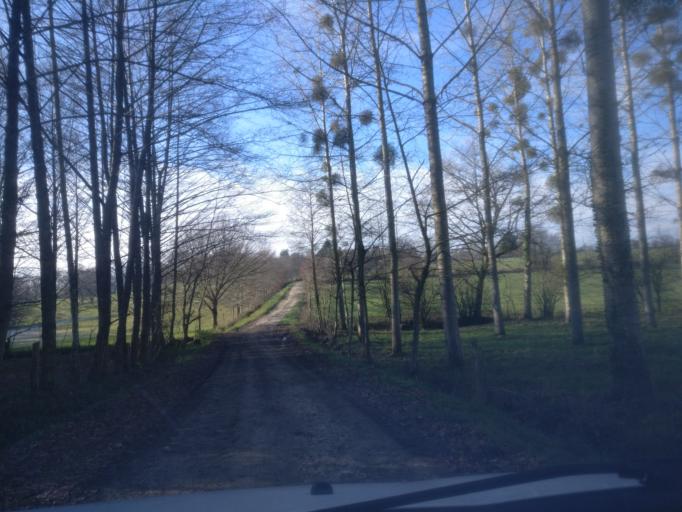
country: FR
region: Brittany
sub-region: Departement d'Ille-et-Vilaine
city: Livre-sur-Changeon
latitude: 48.2358
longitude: -1.3448
